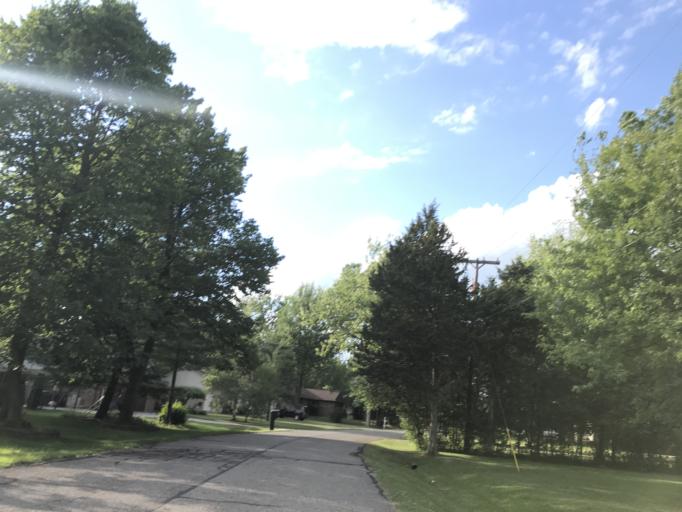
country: US
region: Michigan
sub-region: Oakland County
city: Farmington
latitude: 42.4597
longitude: -83.3285
